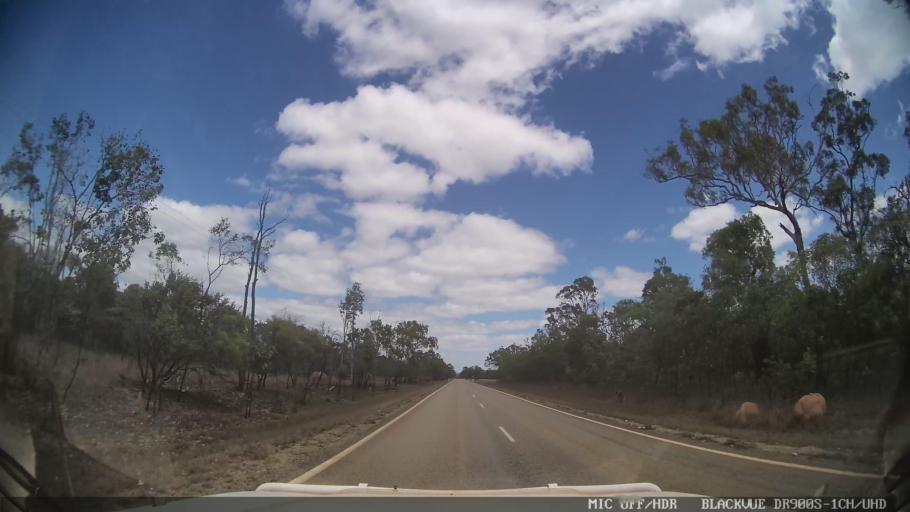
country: AU
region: Queensland
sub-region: Tablelands
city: Ravenshoe
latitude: -17.8154
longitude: 144.9563
